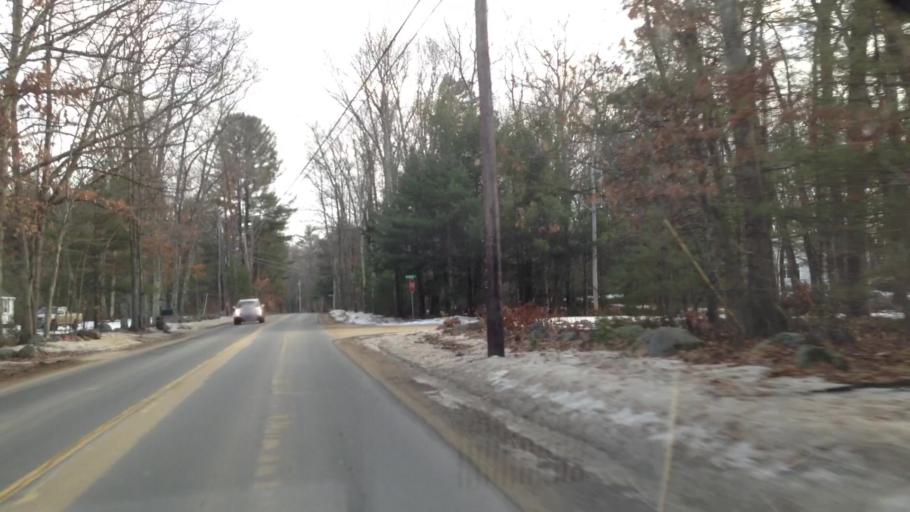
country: US
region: New Hampshire
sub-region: Hillsborough County
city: Merrimack
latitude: 42.8243
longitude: -71.5634
